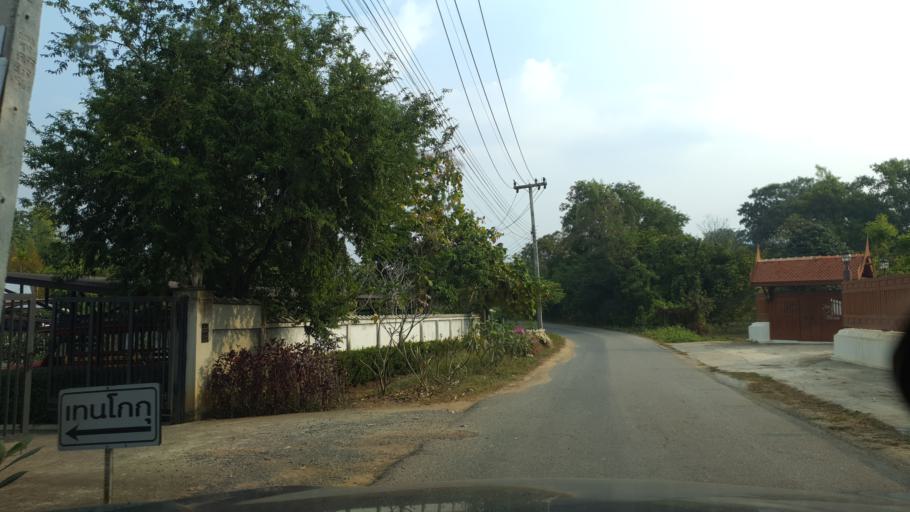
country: TH
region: Chiang Mai
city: Mae On
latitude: 18.7326
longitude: 99.2332
